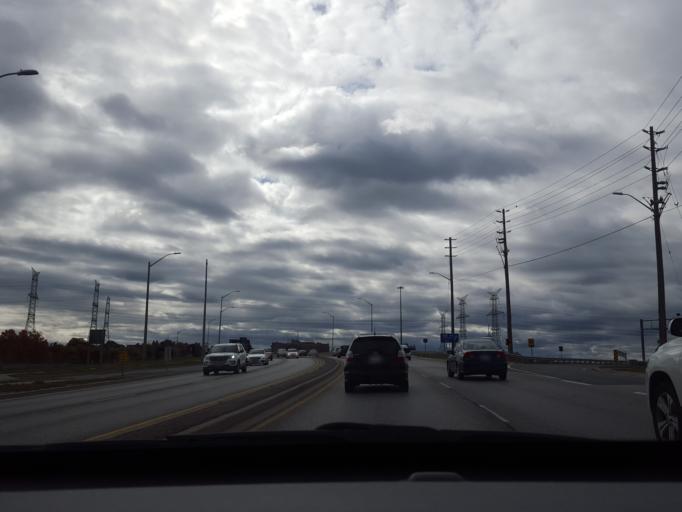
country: CA
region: Ontario
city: Markham
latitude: 43.8517
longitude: -79.3080
